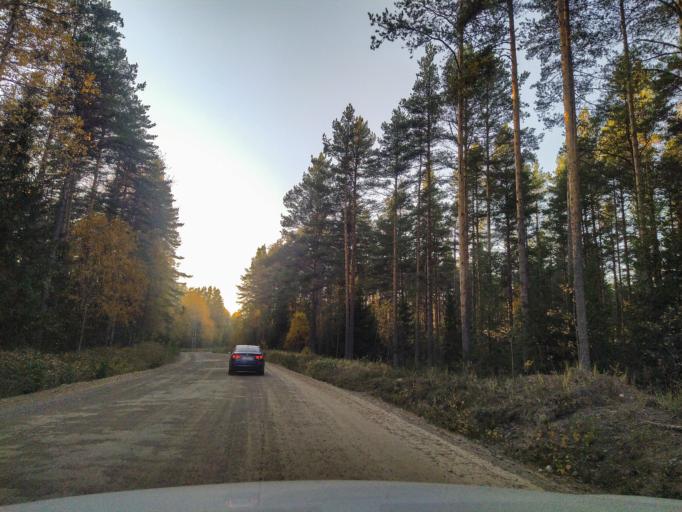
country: RU
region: Leningrad
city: Kuznechnoye
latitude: 61.3290
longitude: 29.9811
